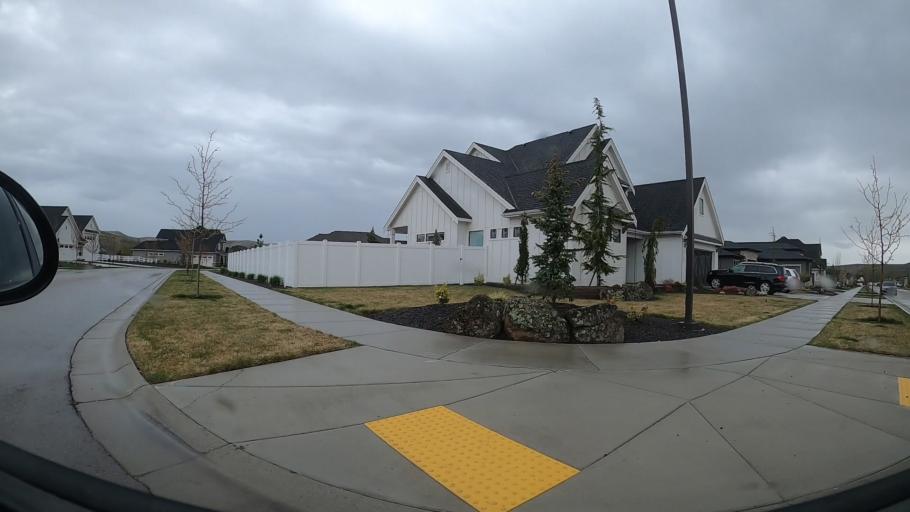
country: US
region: Idaho
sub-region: Ada County
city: Eagle
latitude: 43.7349
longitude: -116.2957
